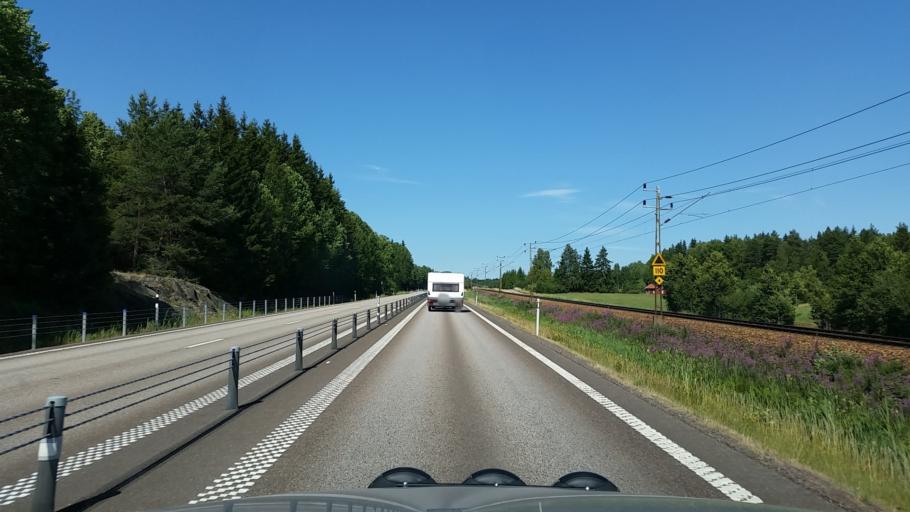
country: SE
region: Vaestra Goetaland
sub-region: Melleruds Kommun
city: Mellerud
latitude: 58.8597
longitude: 12.5586
